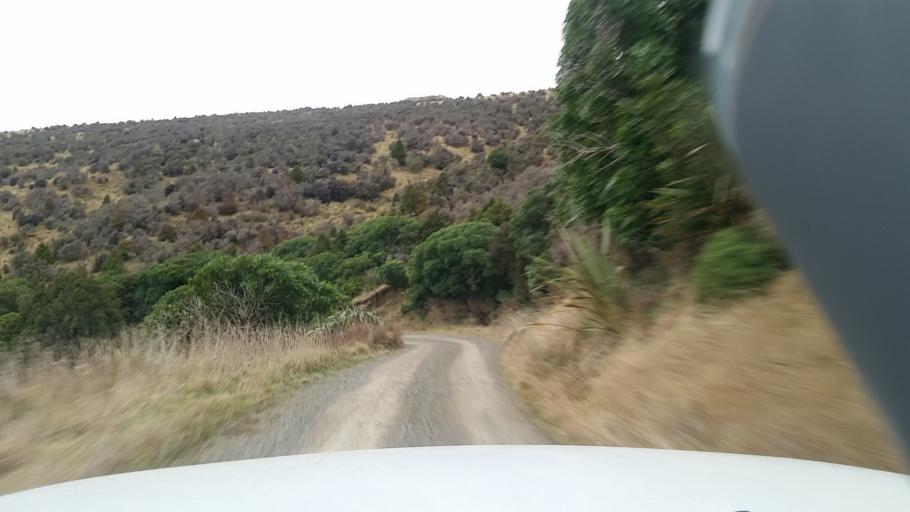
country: NZ
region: Canterbury
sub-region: Christchurch City
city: Christchurch
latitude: -43.8169
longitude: 172.7828
